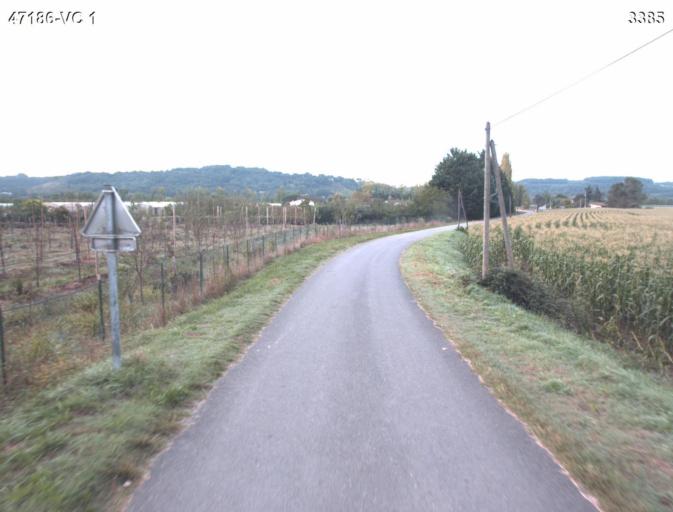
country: FR
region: Aquitaine
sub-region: Departement du Lot-et-Garonne
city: Port-Sainte-Marie
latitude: 44.2168
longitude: 0.4431
